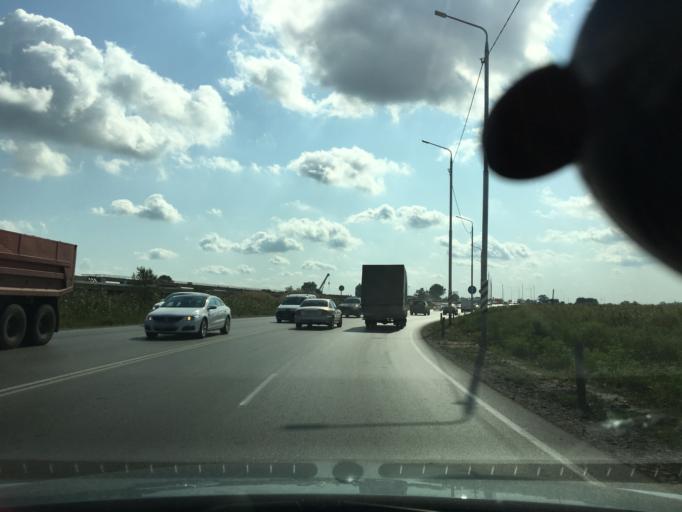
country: RU
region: Rostov
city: Rostov-na-Donu
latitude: 47.2011
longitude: 39.7256
